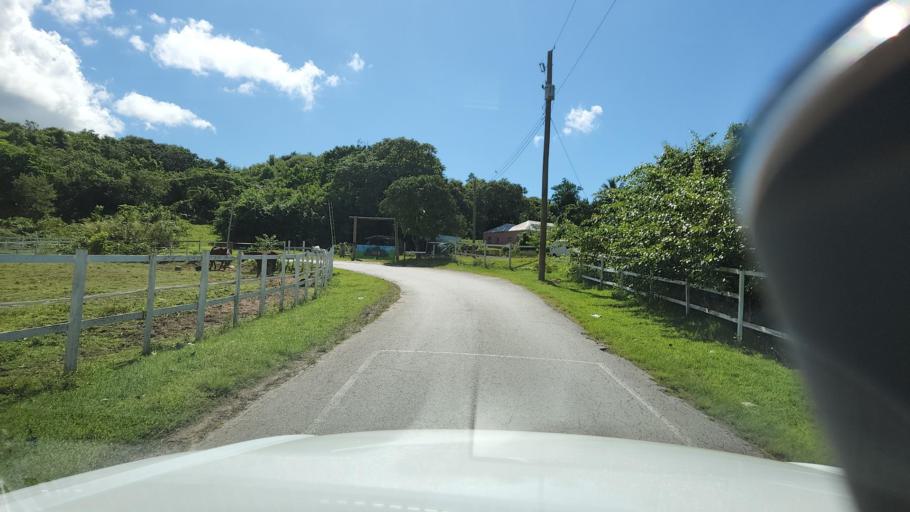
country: BB
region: Saint Andrew
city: Greenland
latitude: 13.2277
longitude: -59.5631
